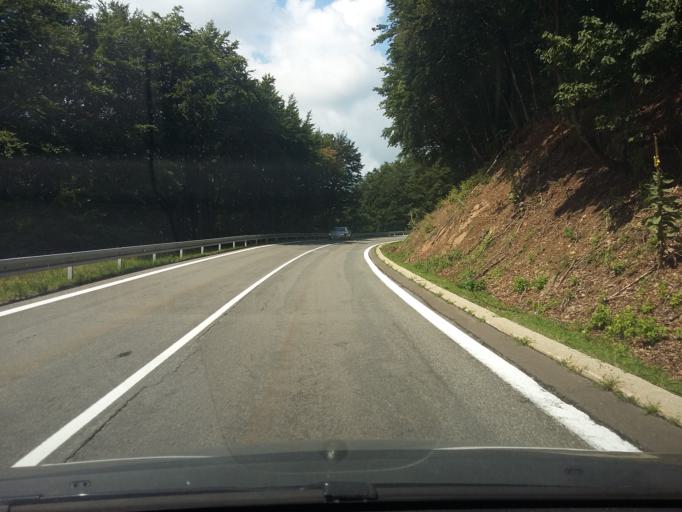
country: SK
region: Bratislavsky
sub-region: Okres Pezinok
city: Pezinok
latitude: 48.3500
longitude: 17.2002
